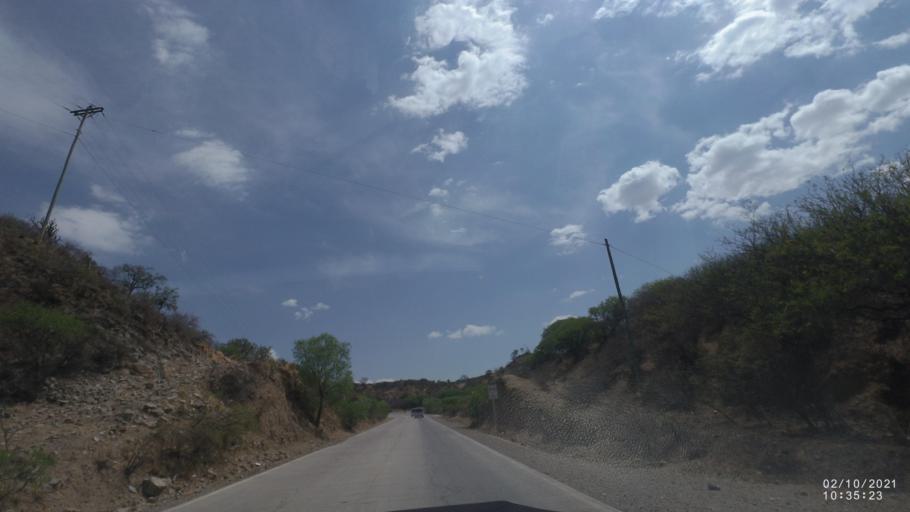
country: BO
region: Cochabamba
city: Capinota
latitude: -17.6618
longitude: -66.2577
